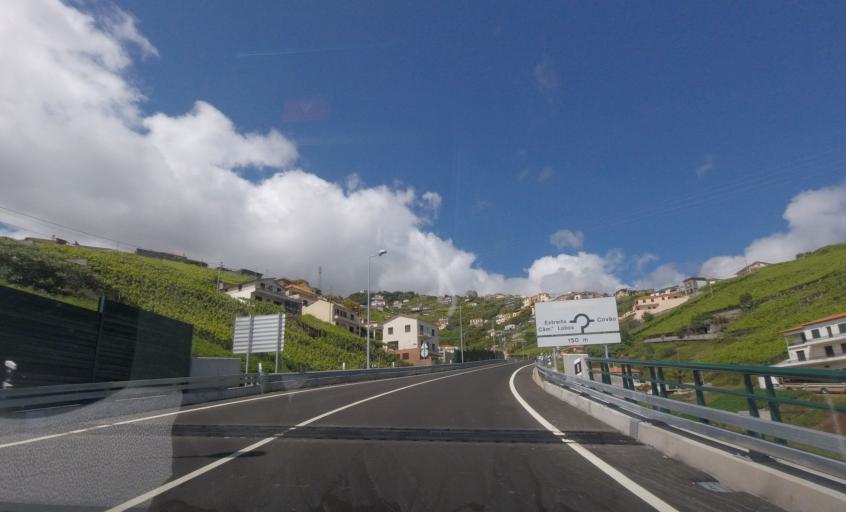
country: PT
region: Madeira
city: Camara de Lobos
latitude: 32.6731
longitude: -16.9744
